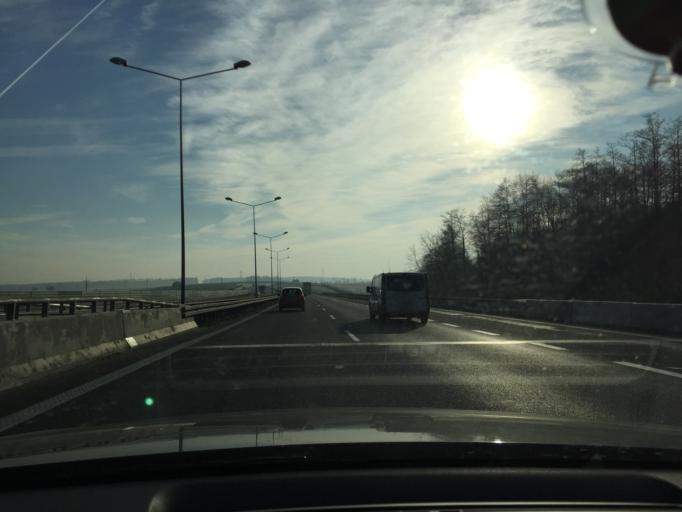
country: PL
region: Silesian Voivodeship
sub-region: Powiat gliwicki
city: Sosnicowice
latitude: 50.3064
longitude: 18.5523
